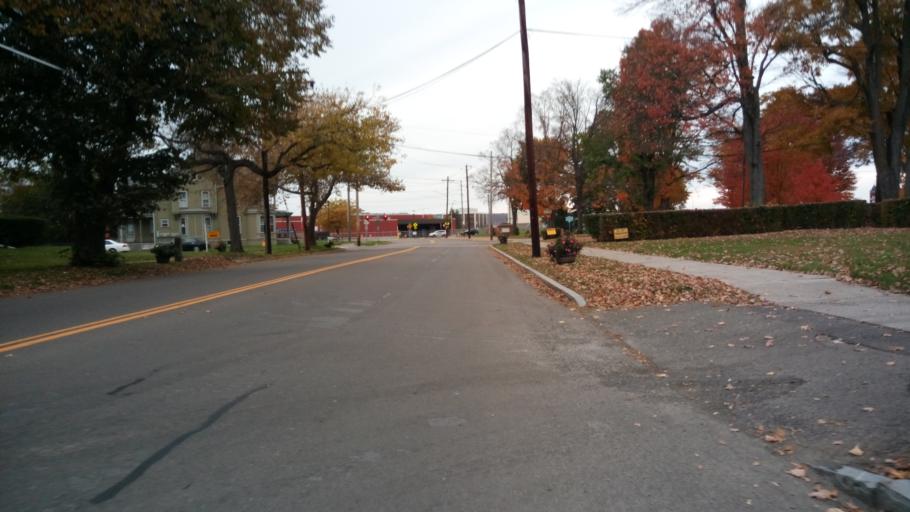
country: US
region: New York
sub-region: Chemung County
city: Elmira
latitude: 42.0848
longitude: -76.7971
